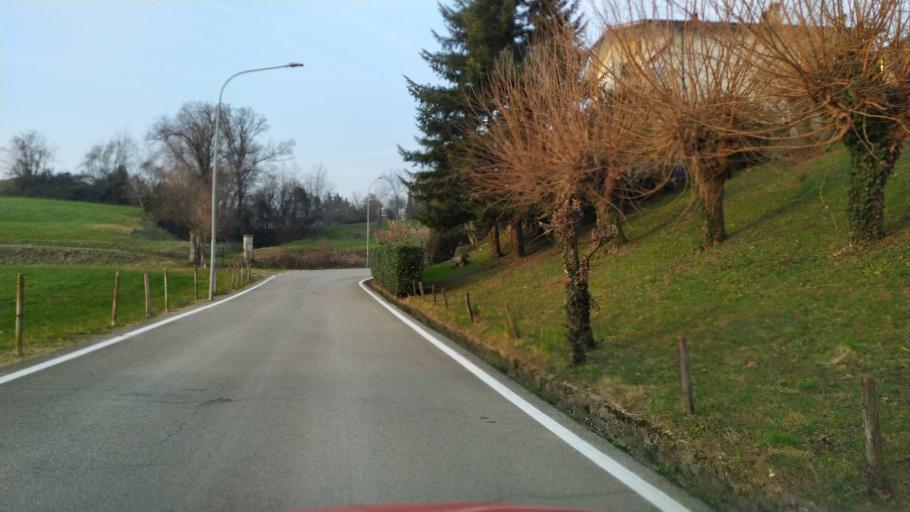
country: IT
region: Veneto
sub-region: Provincia di Vicenza
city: Sarcedo
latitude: 45.7034
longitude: 11.5243
